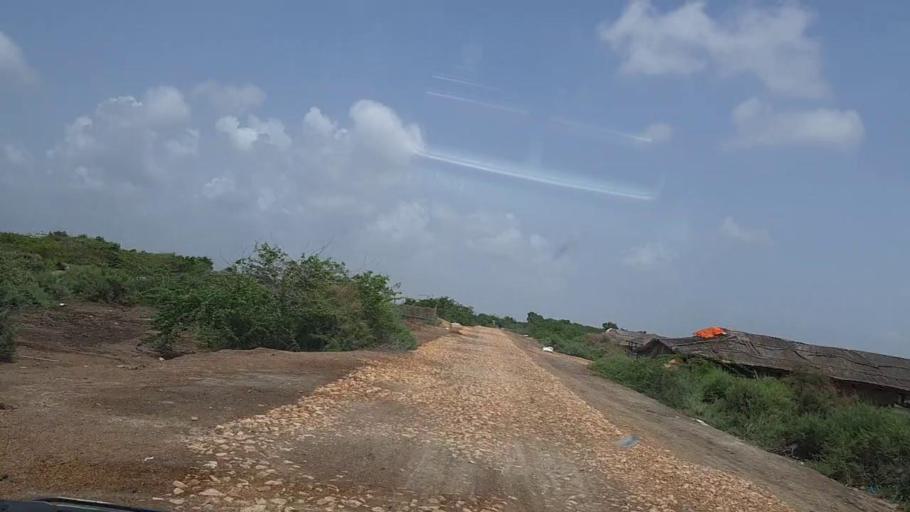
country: PK
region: Sindh
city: Keti Bandar
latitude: 24.1525
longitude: 67.5377
